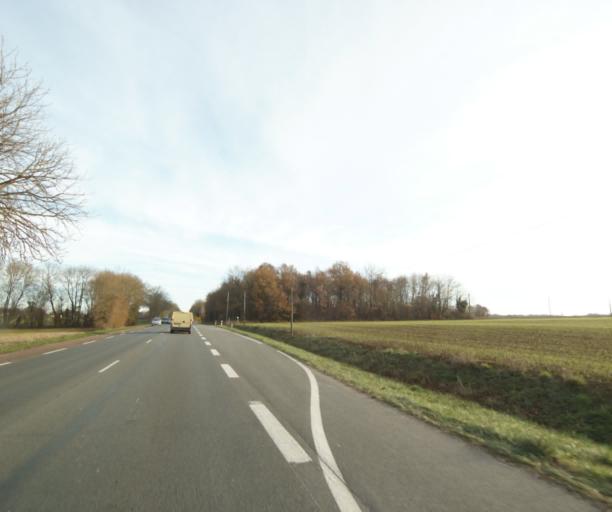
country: FR
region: Poitou-Charentes
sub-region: Departement de la Charente-Maritime
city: Saint-Georges-des-Coteaux
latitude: 45.7825
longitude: -0.7099
